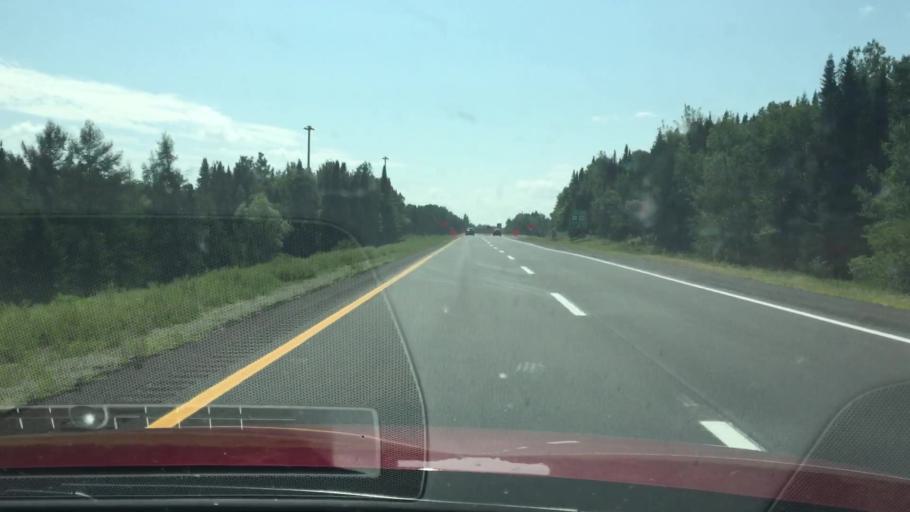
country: US
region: Maine
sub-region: Penobscot County
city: Patten
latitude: 45.8787
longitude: -68.4106
